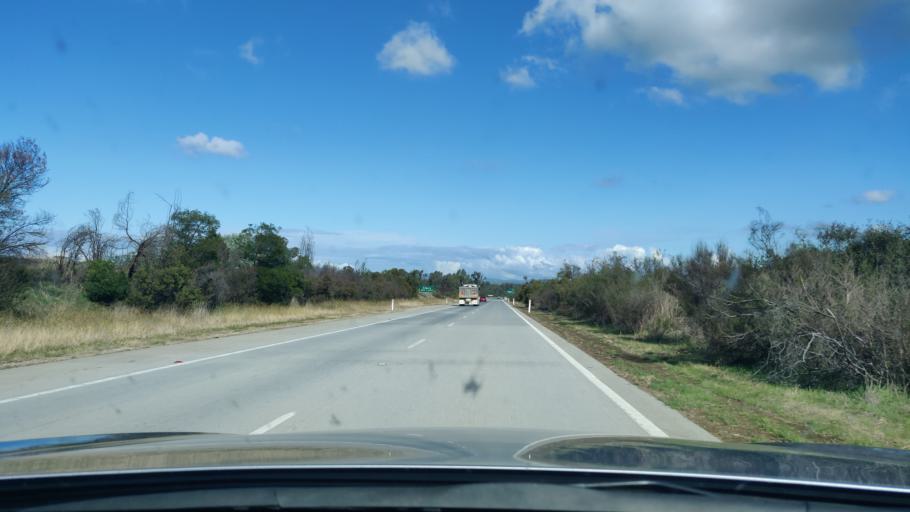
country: AU
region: New South Wales
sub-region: Albury Municipality
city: Lavington
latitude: -36.0133
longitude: 146.9870
